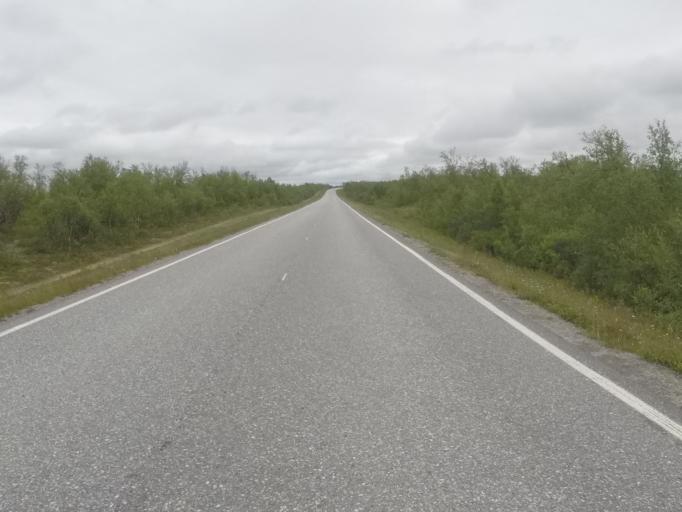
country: NO
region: Finnmark Fylke
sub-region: Kautokeino
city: Kautokeino
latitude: 69.0568
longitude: 23.1281
